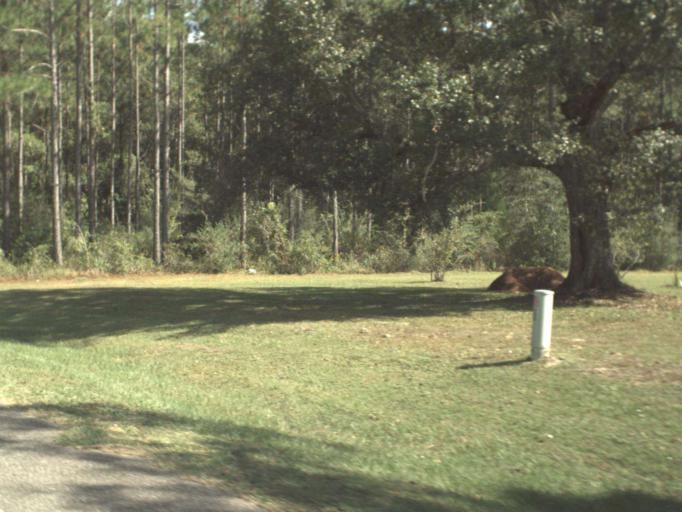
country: US
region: Florida
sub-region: Walton County
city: DeFuniak Springs
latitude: 30.8378
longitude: -86.1187
